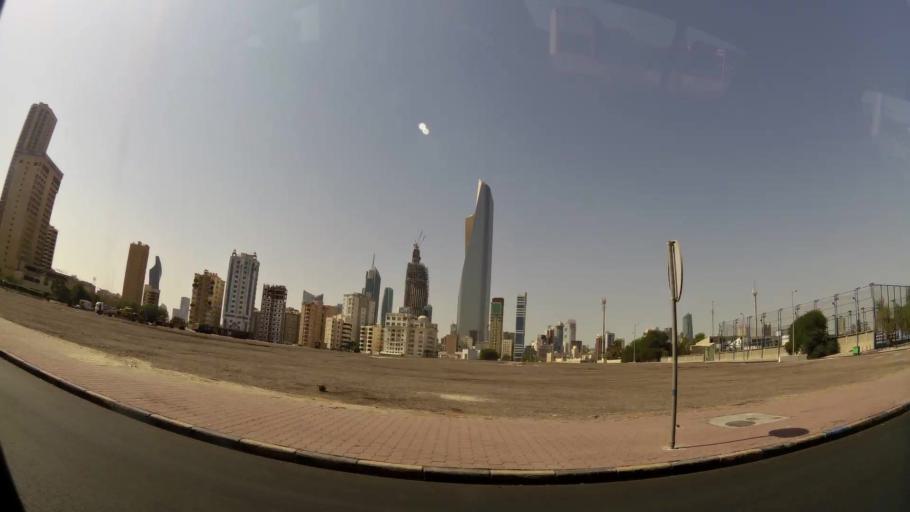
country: KW
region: Al Asimah
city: Ad Dasmah
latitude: 29.3800
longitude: 48.0030
